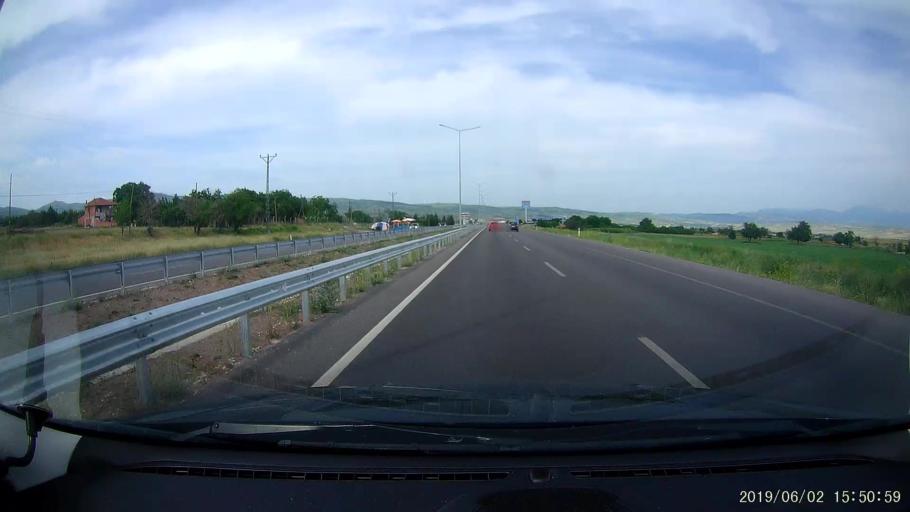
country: TR
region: Amasya
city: Merzifon
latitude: 40.8638
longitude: 35.4883
